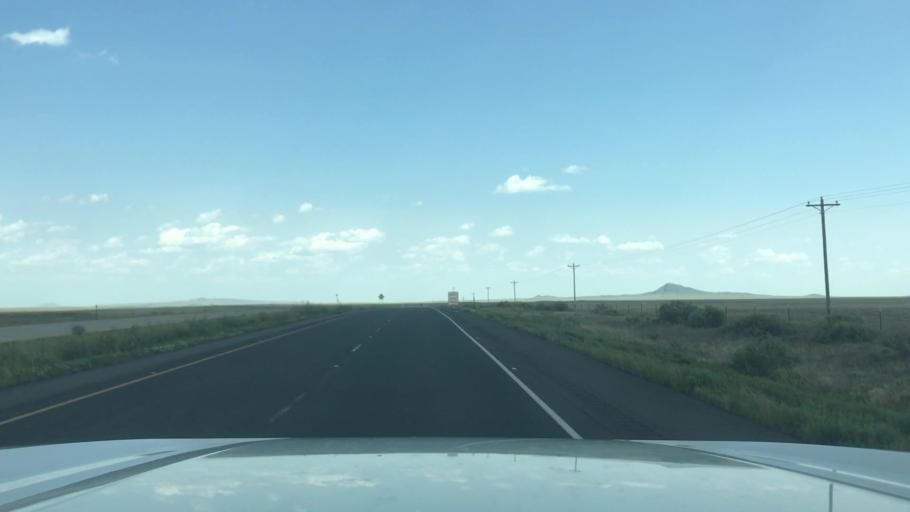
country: US
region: New Mexico
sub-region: Union County
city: Clayton
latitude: 36.6237
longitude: -103.7010
